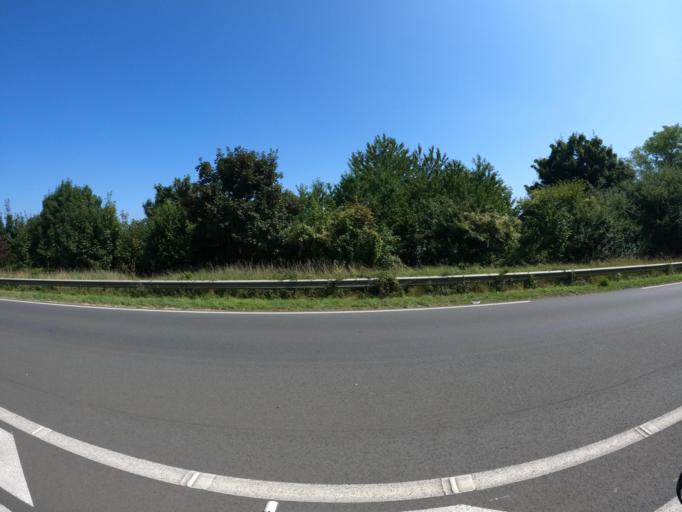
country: FR
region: Poitou-Charentes
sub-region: Departement des Deux-Sevres
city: Celles-sur-Belle
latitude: 46.2573
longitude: -0.2262
